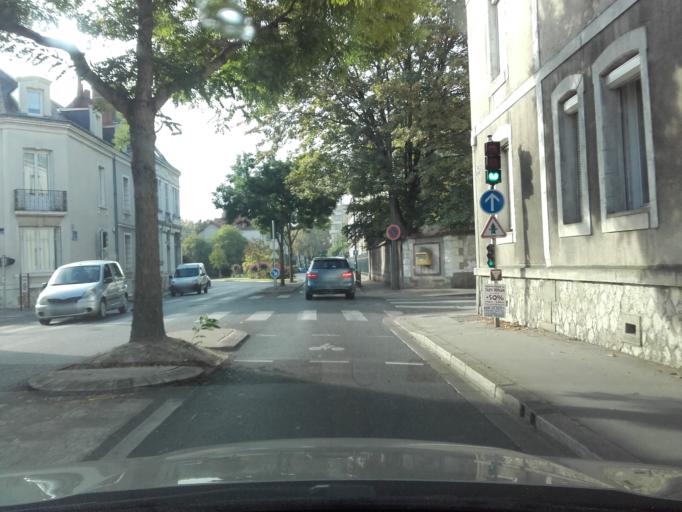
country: FR
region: Centre
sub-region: Departement d'Indre-et-Loire
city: Tours
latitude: 47.3945
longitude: 0.7000
